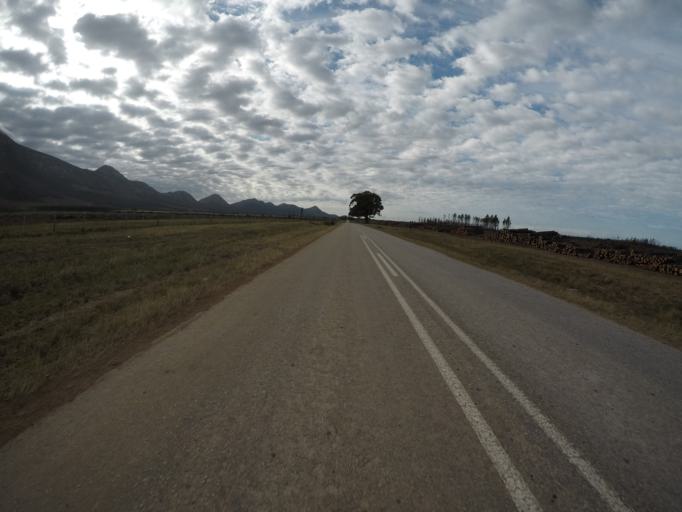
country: ZA
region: Eastern Cape
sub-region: Cacadu District Municipality
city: Kareedouw
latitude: -34.0425
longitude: 24.4166
